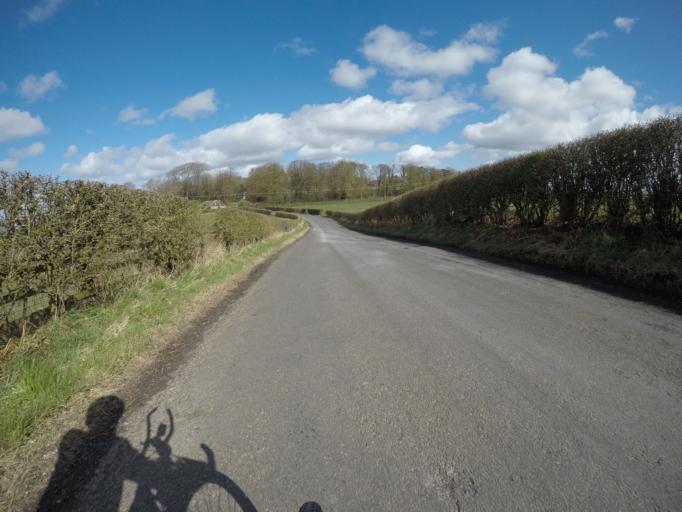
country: GB
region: Scotland
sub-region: North Ayrshire
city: Springside
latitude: 55.6100
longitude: -4.5759
